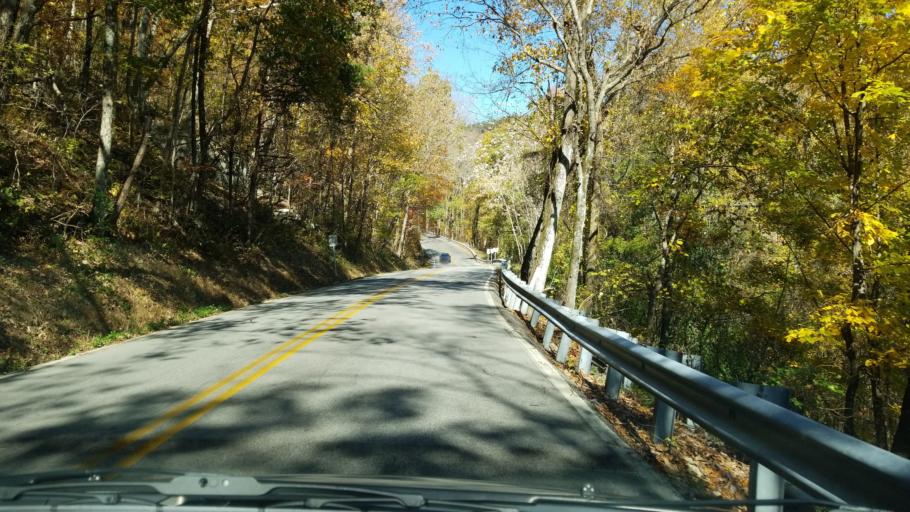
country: US
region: Tennessee
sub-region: Hamilton County
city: Falling Water
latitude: 35.2119
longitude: -85.2607
